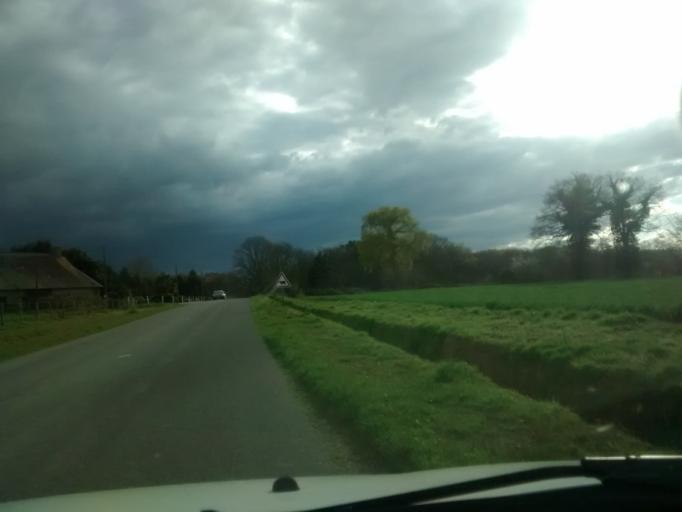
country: FR
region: Brittany
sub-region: Departement d'Ille-et-Vilaine
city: La Bouexiere
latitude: 48.1680
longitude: -1.4760
